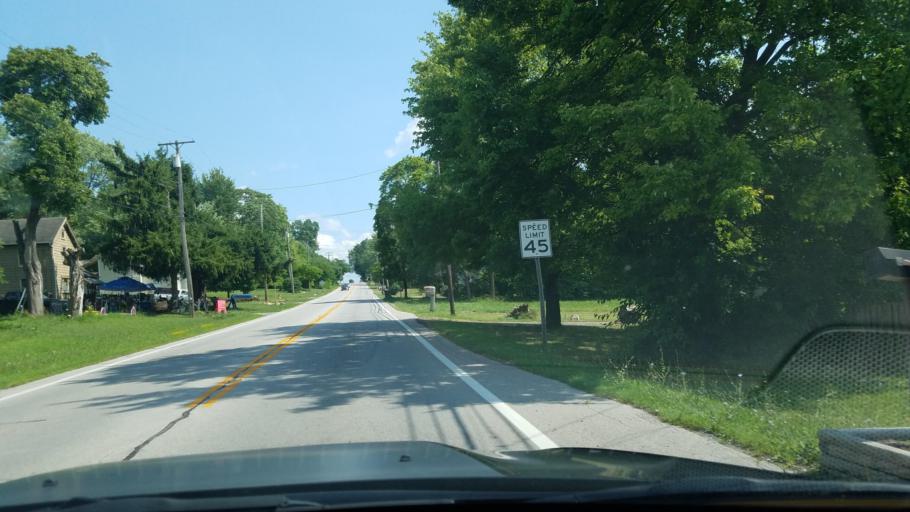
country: US
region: Ohio
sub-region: Trumbull County
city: Bolindale
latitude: 41.2098
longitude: -80.7859
